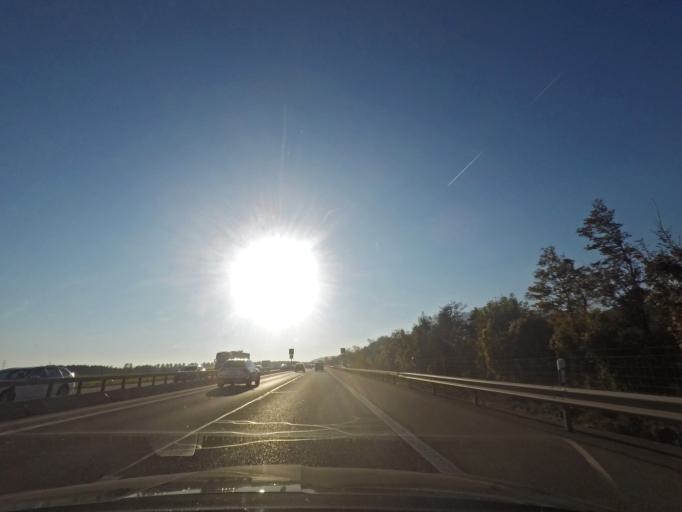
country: CH
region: Solothurn
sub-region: Bezirk Gaeu
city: Oensingen
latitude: 47.2927
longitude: 7.7436
